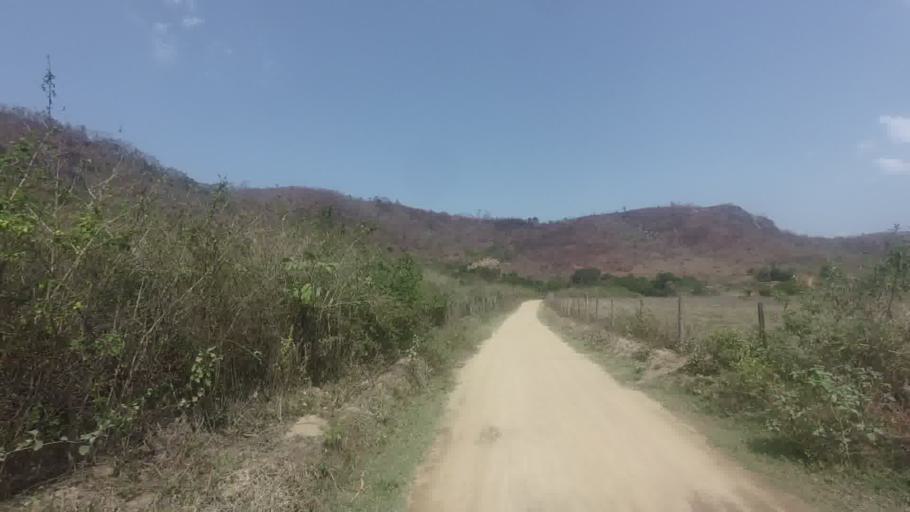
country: BR
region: Espirito Santo
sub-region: Sao Jose Do Calcado
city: Sao Jose do Calcado
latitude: -21.0261
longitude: -41.5176
